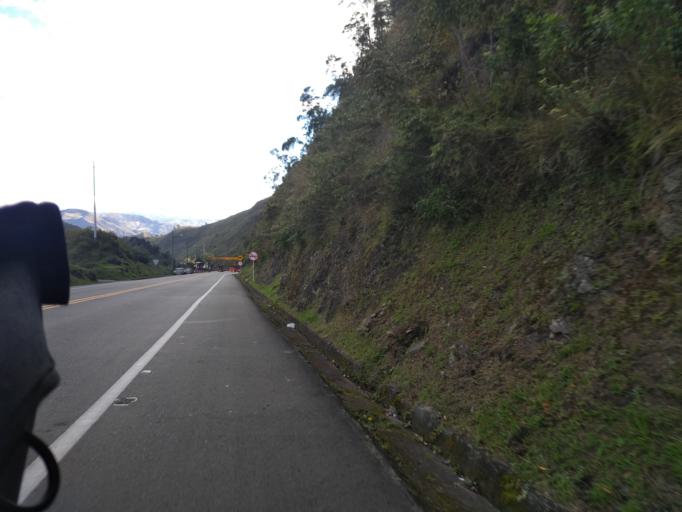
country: CO
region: Narino
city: Tangua
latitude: 1.0880
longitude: -77.4065
